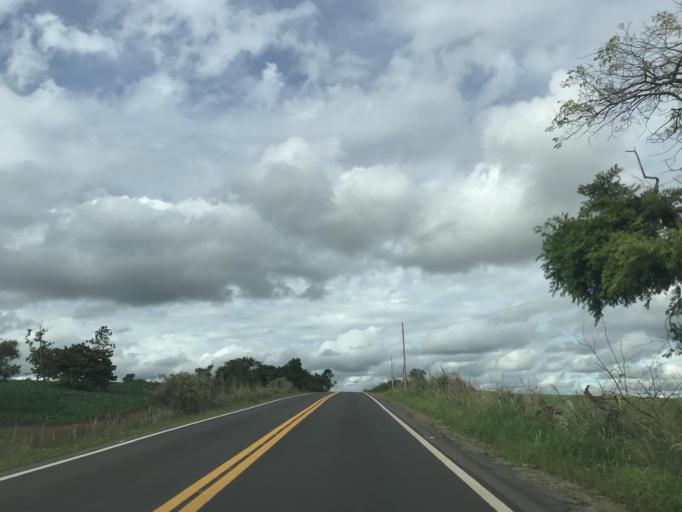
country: BR
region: Goias
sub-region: Bela Vista De Goias
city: Bela Vista de Goias
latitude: -17.1909
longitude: -48.6951
